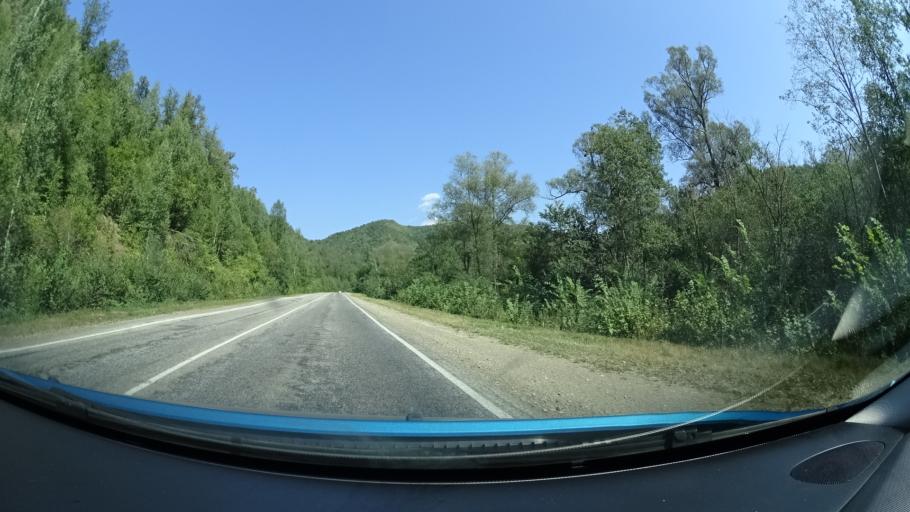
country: RU
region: Bashkortostan
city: Inzer
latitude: 54.3329
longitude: 57.1350
